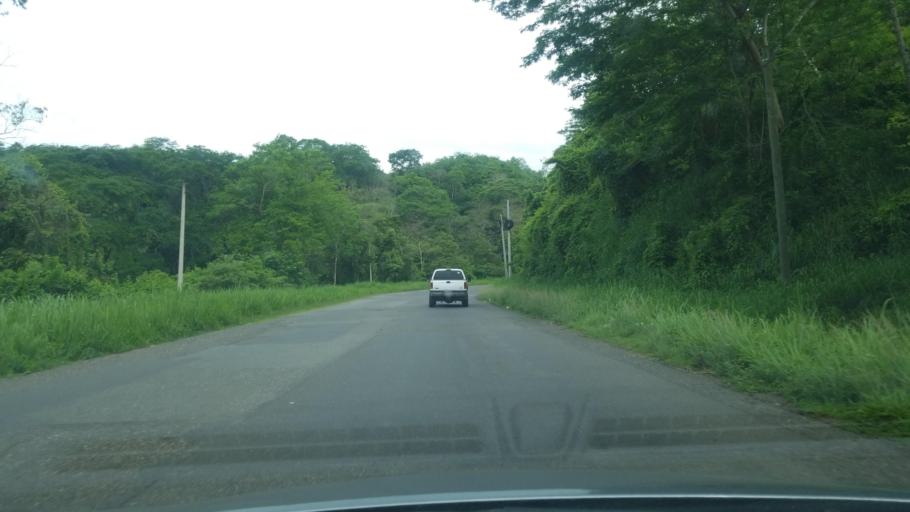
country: HN
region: Santa Barbara
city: Camalote
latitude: 15.3271
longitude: -88.2909
